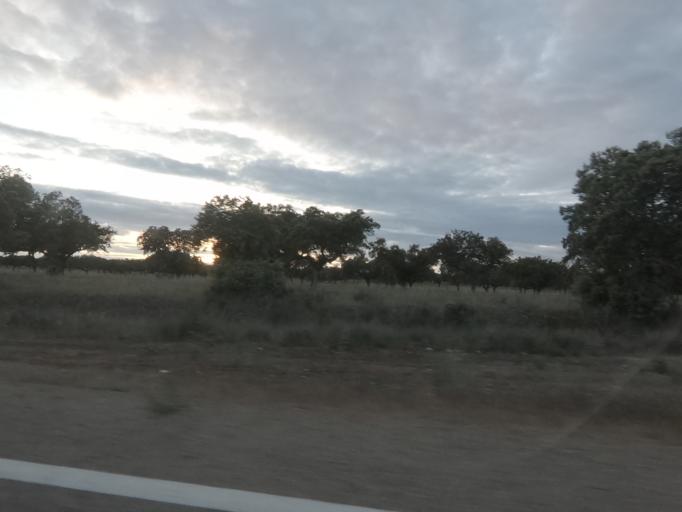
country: ES
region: Extremadura
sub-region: Provincia de Badajoz
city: Villar del Rey
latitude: 39.0376
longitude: -6.8171
